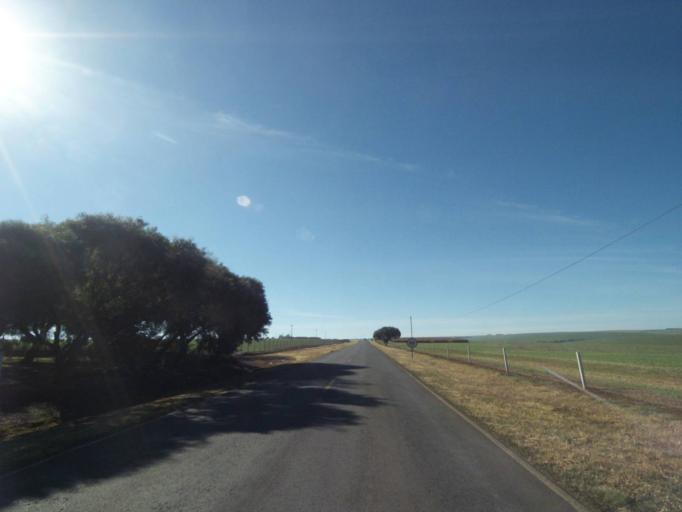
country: BR
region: Parana
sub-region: Tibagi
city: Tibagi
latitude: -24.5248
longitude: -50.3715
